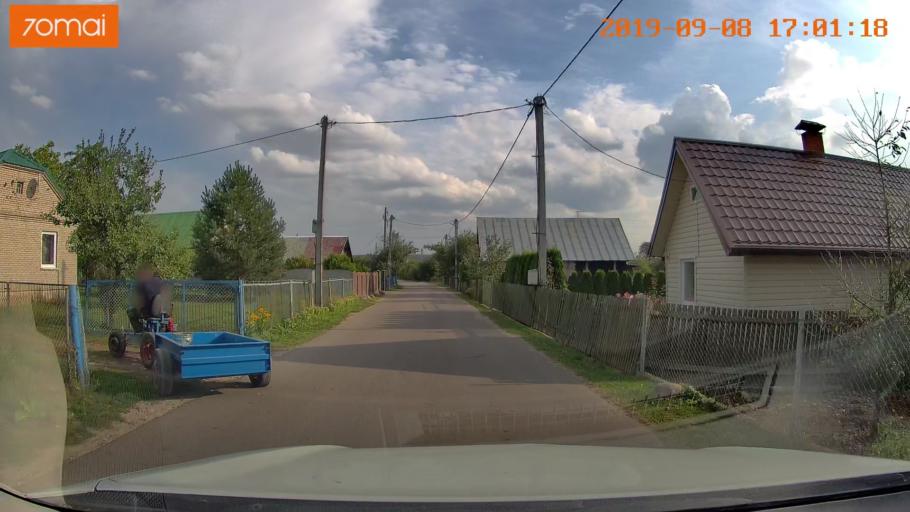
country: BY
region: Grodnenskaya
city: Hrodna
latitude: 53.7112
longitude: 23.9340
